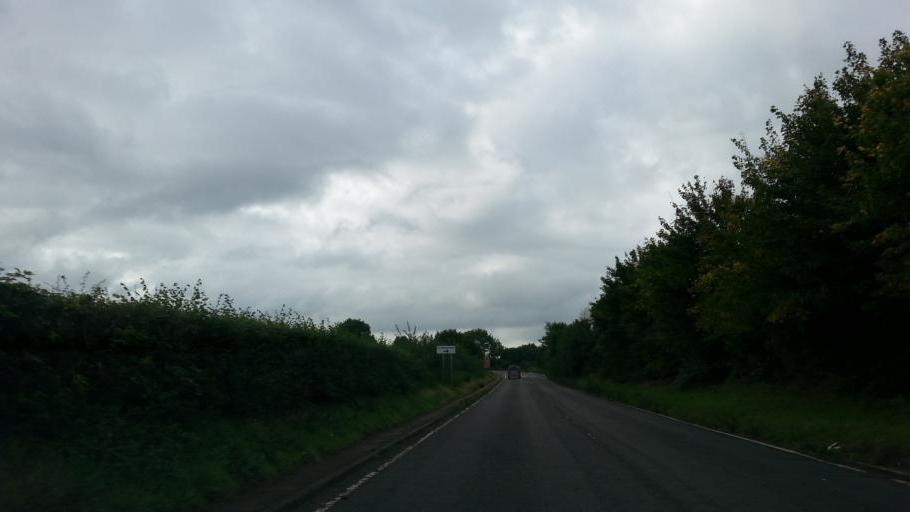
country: GB
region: England
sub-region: Hertfordshire
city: Hitchin
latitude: 51.9818
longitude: -0.2899
